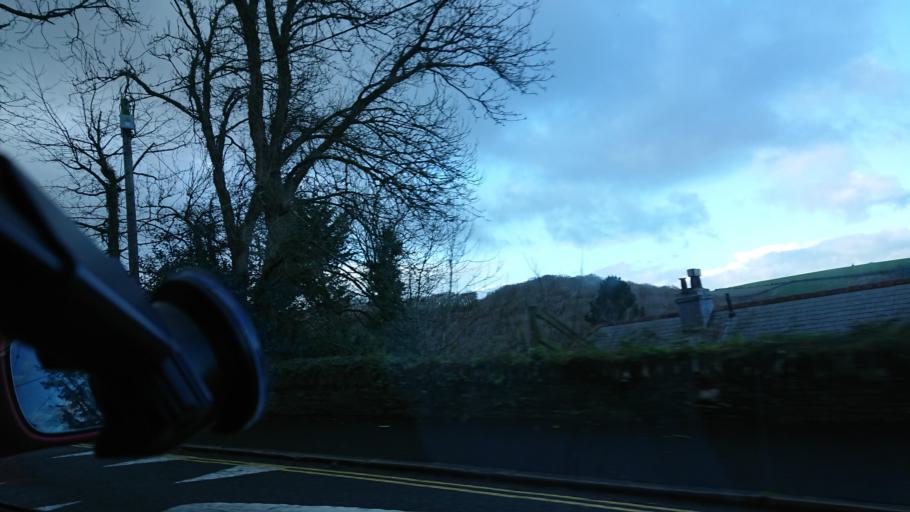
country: GB
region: England
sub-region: Cornwall
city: Looe
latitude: 50.3558
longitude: -4.4639
